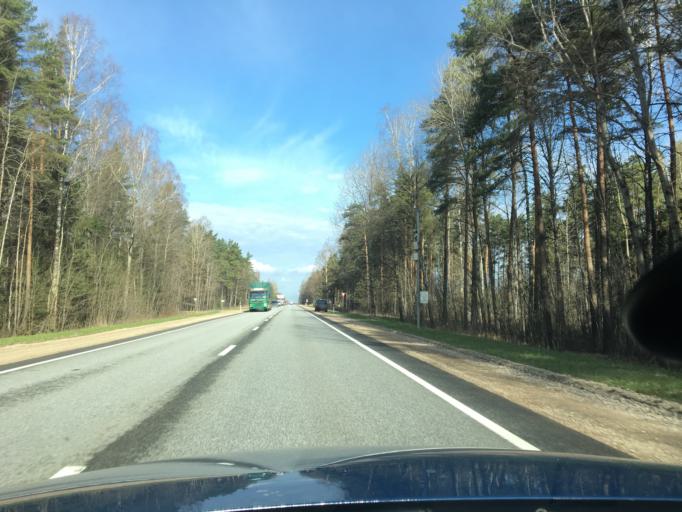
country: LV
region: Marupe
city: Marupe
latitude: 56.8431
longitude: 24.0200
